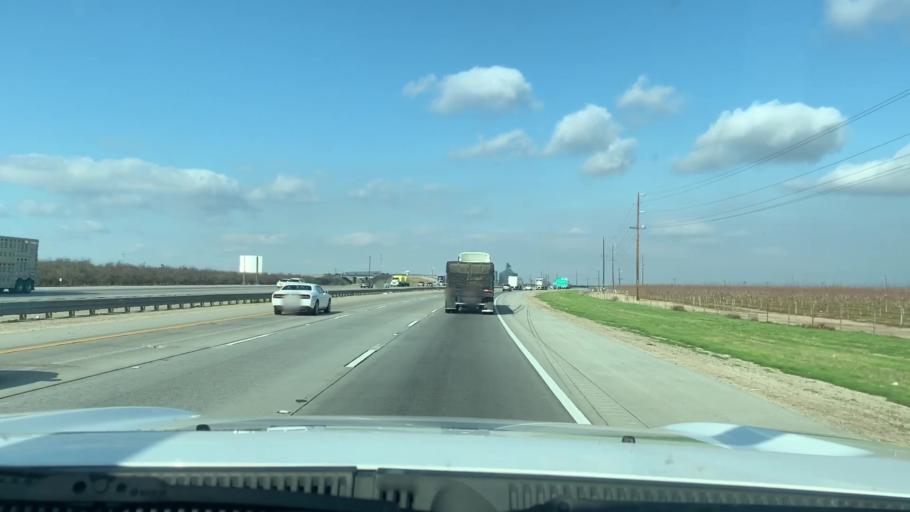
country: US
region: California
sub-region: Kern County
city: McFarland
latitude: 35.5841
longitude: -119.2040
